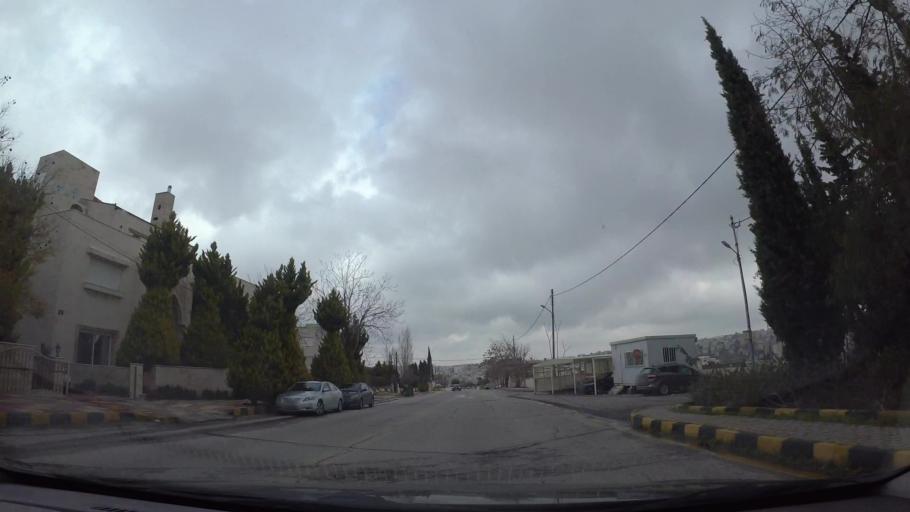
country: JO
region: Amman
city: Amman
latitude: 31.9442
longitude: 35.8971
